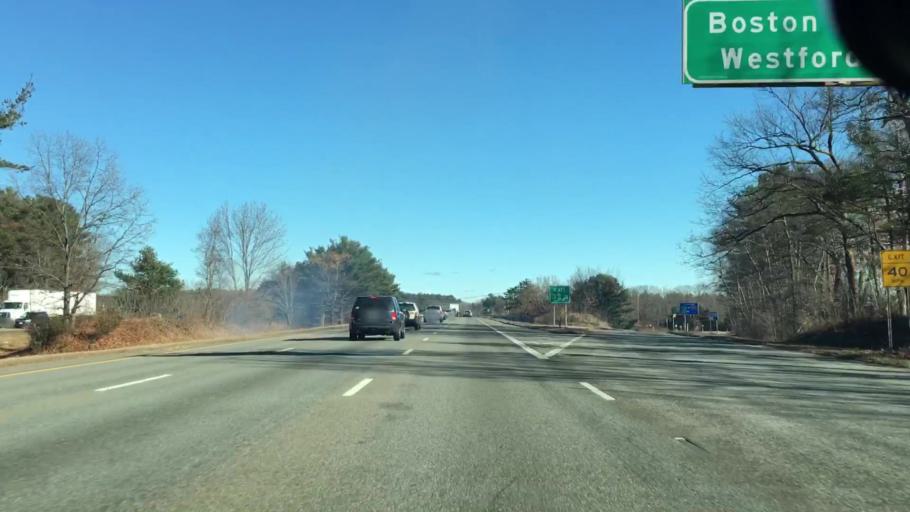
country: US
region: Massachusetts
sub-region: Middlesex County
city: Westford
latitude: 42.5667
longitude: -71.4287
